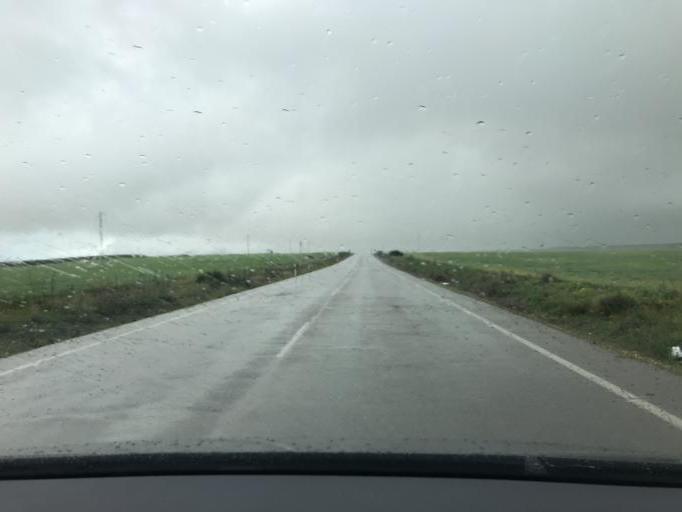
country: ES
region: Andalusia
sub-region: Provincia de Sevilla
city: La Luisiana
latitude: 37.4584
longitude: -5.2217
